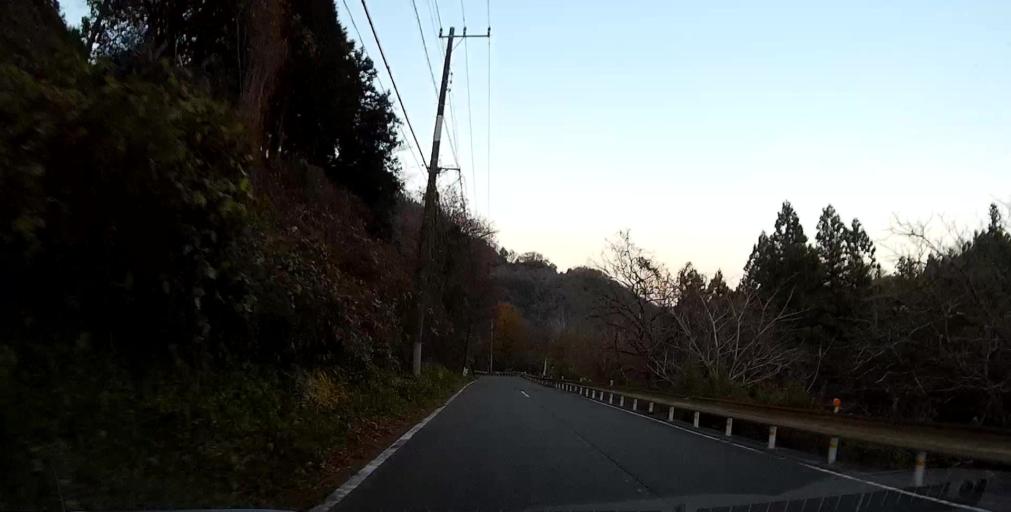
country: JP
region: Yamanashi
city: Uenohara
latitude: 35.5649
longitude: 139.2080
